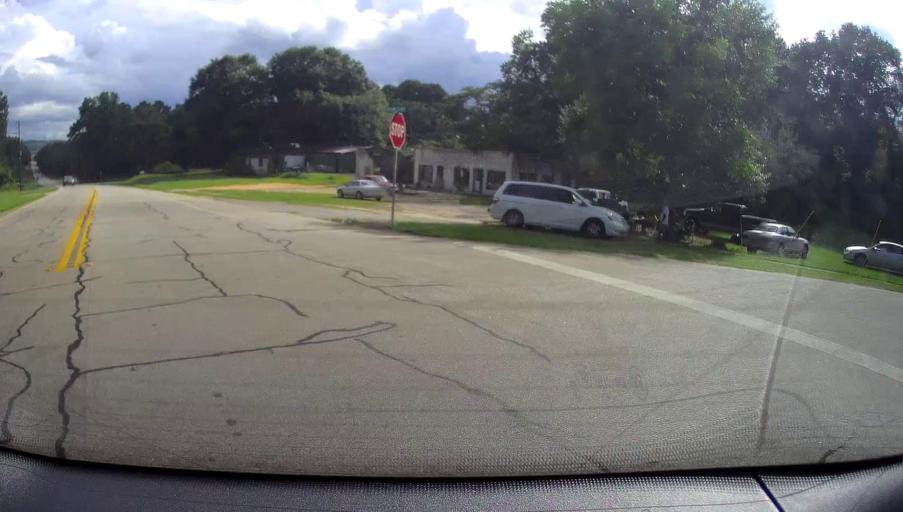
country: US
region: Georgia
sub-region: Meriwether County
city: Manchester
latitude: 32.9756
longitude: -84.5779
